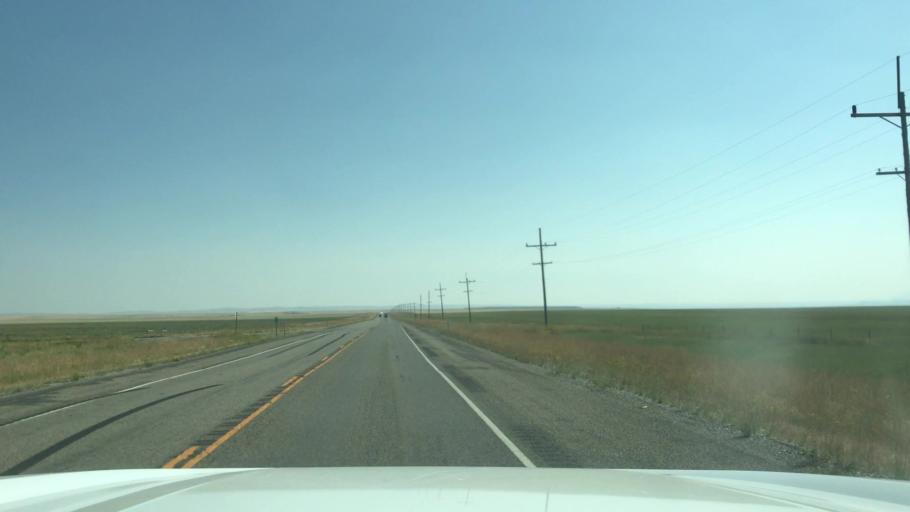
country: US
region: Montana
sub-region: Wheatland County
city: Harlowton
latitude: 46.5200
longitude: -109.7661
